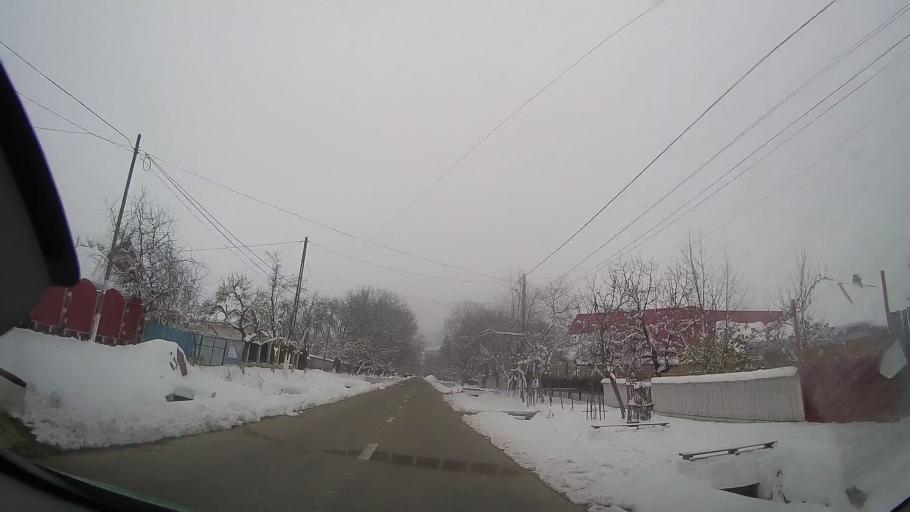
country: RO
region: Vaslui
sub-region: Comuna Bacesti
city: Bacesti
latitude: 46.8207
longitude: 27.2027
